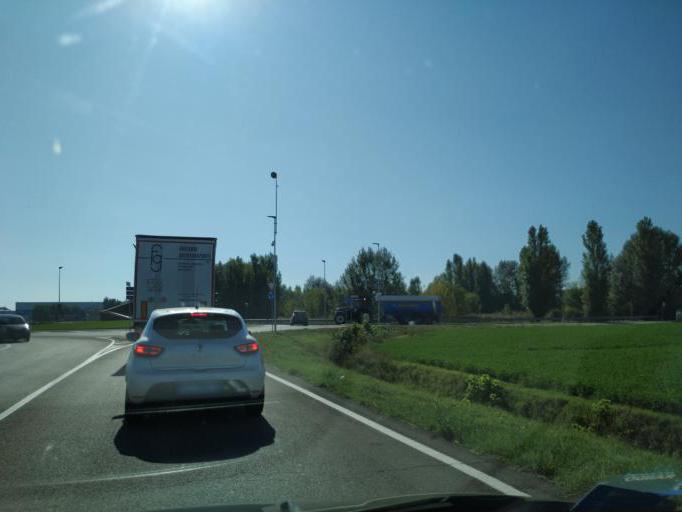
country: IT
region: Emilia-Romagna
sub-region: Provincia di Bologna
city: Sant'Agata Bolognese
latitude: 44.6628
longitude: 11.1161
